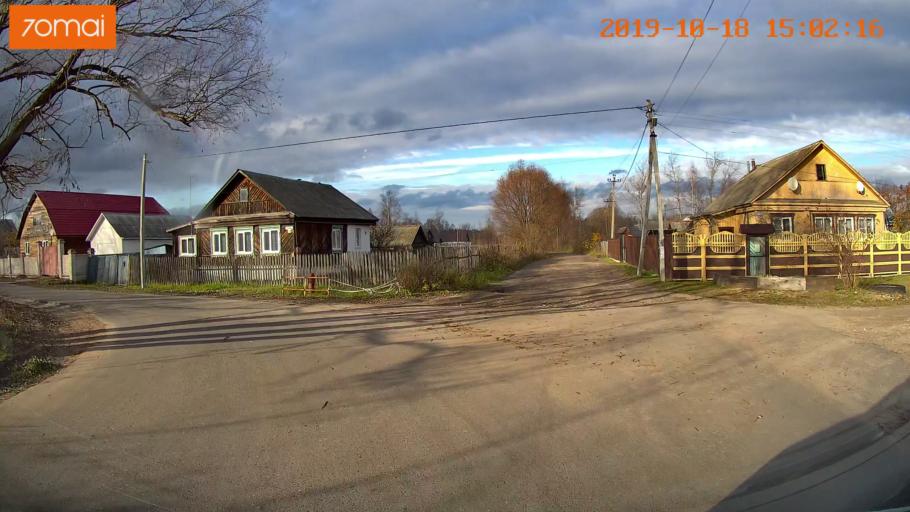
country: RU
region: Vladimir
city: Gus'-Khrustal'nyy
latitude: 55.5026
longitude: 40.6083
